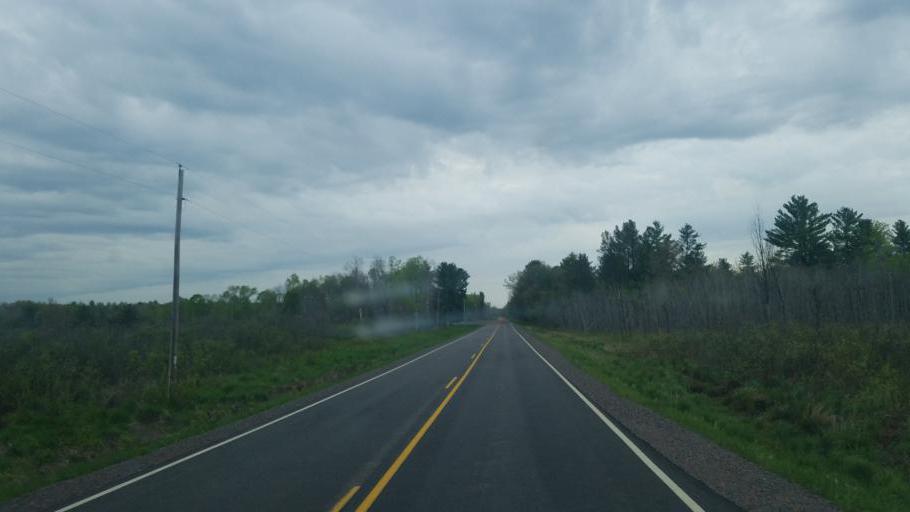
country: US
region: Wisconsin
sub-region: Wood County
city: Marshfield
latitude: 44.5090
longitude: -90.2792
